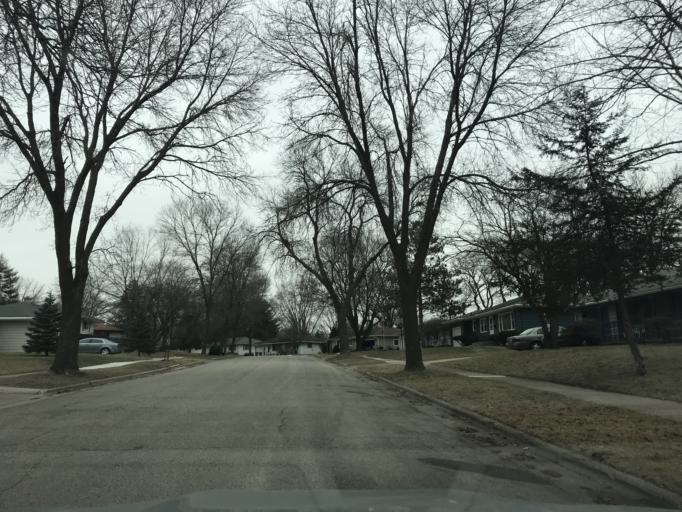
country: US
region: Wisconsin
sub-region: Dane County
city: Monona
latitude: 43.0869
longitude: -89.3028
